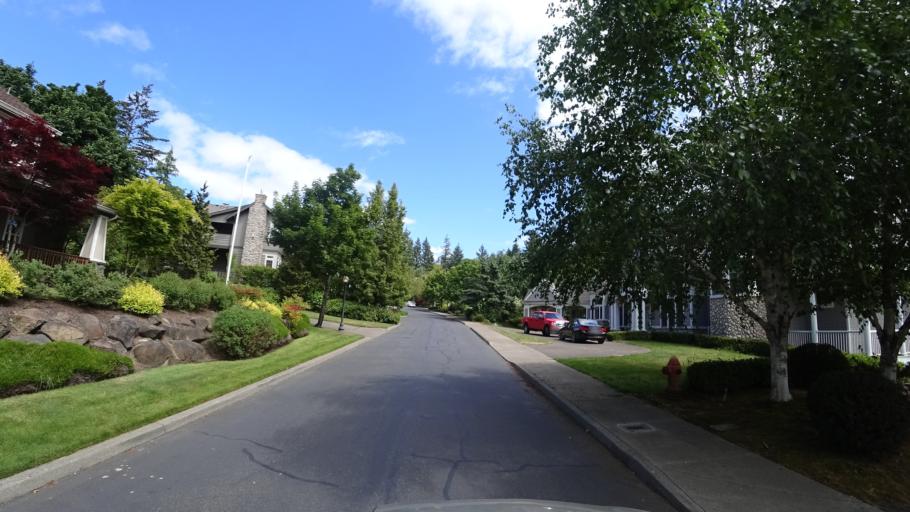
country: US
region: Oregon
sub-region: Washington County
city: Oak Hills
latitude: 45.5962
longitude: -122.8194
